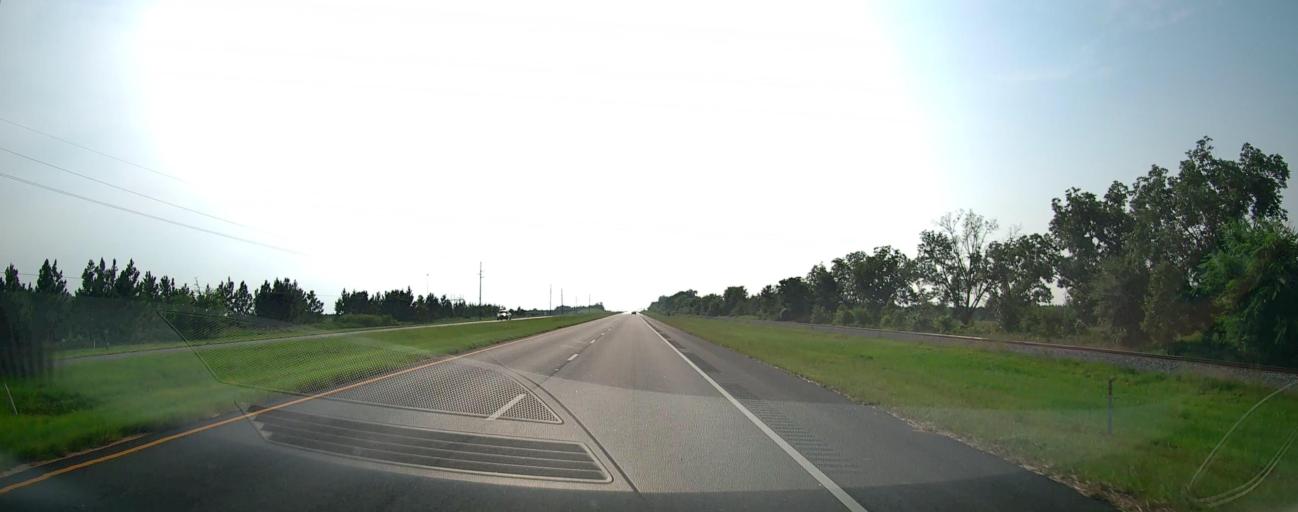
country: US
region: Georgia
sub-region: Taylor County
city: Butler
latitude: 32.5767
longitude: -84.3079
